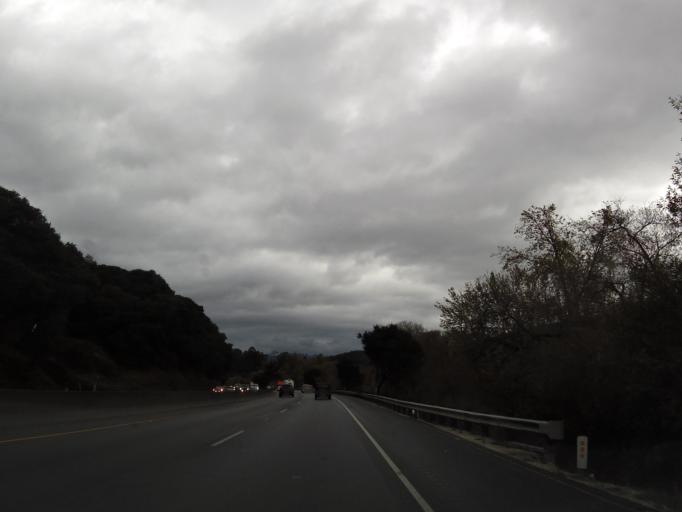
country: US
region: California
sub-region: San Benito County
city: Aromas
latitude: 36.8344
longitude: -121.6301
